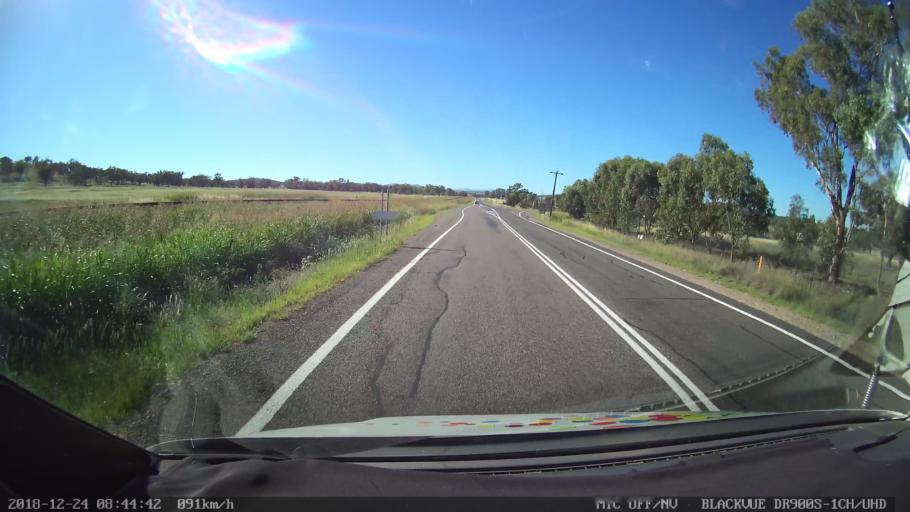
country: AU
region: New South Wales
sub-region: Liverpool Plains
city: Quirindi
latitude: -31.4053
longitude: 150.6495
